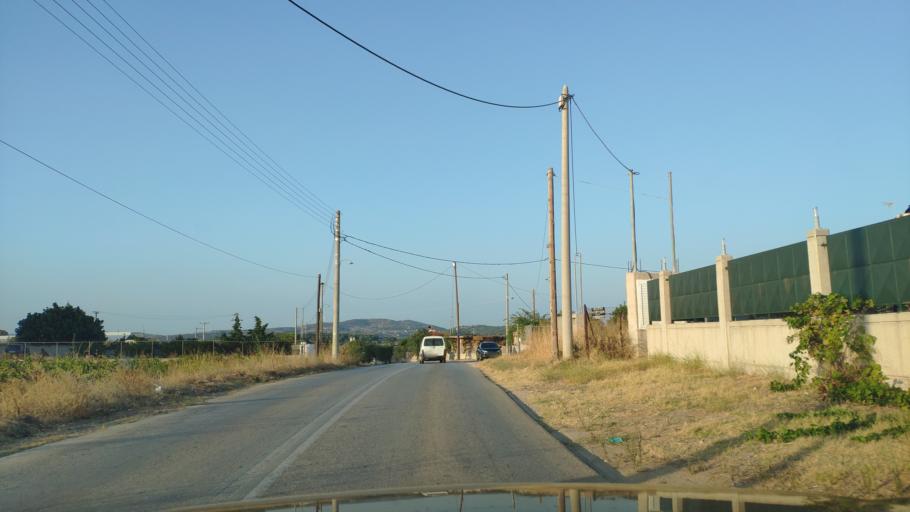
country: GR
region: Attica
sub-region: Nomarchia Anatolikis Attikis
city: Markopoulo
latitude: 37.9051
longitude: 23.9610
